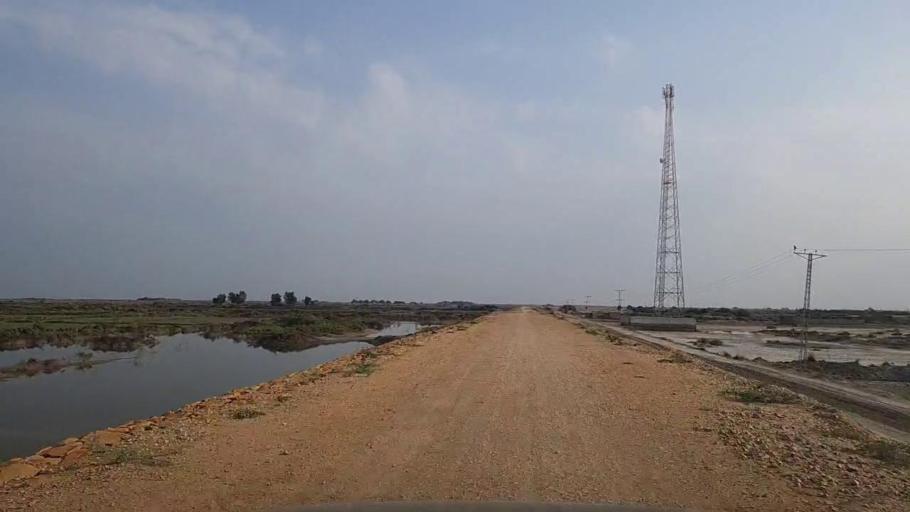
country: PK
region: Sindh
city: Thatta
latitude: 24.6178
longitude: 67.9616
